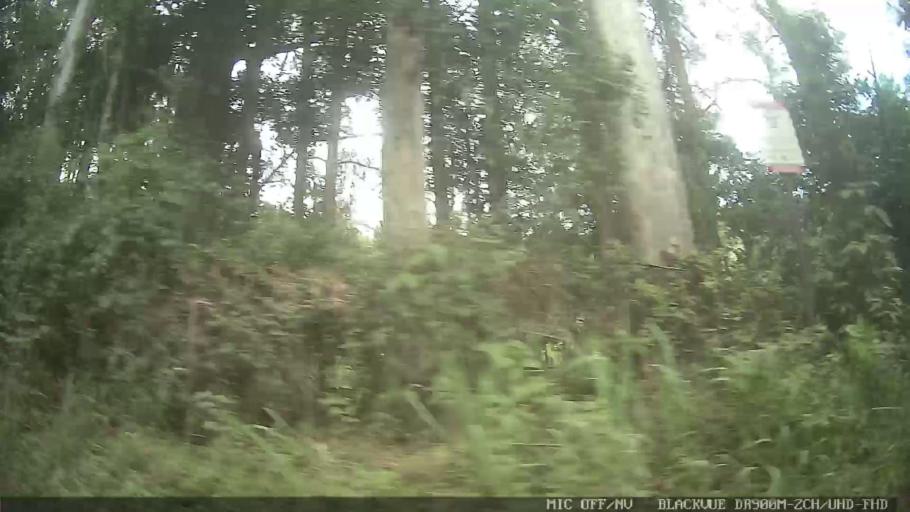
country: BR
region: Sao Paulo
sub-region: Bom Jesus Dos Perdoes
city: Bom Jesus dos Perdoes
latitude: -23.1435
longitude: -46.5114
